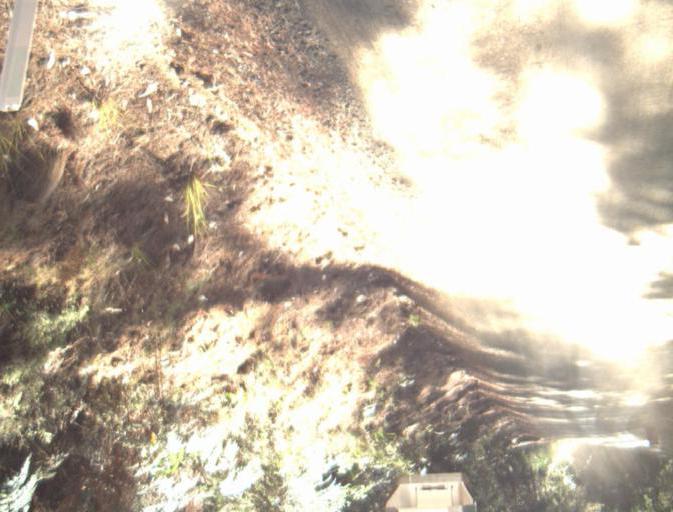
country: AU
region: Tasmania
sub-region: Launceston
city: Mayfield
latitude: -41.3048
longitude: 147.1974
